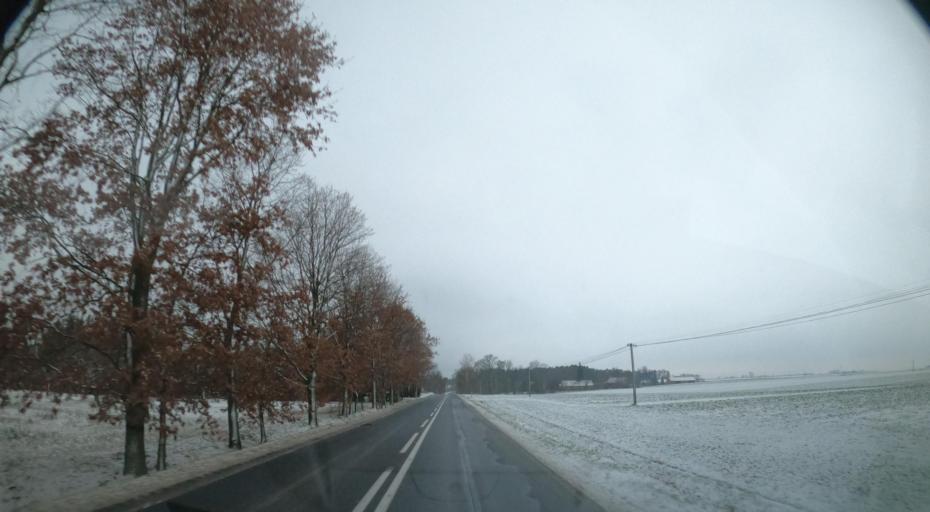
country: PL
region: Masovian Voivodeship
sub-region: Powiat plocki
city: Nowy Duninow
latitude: 52.6080
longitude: 19.4802
